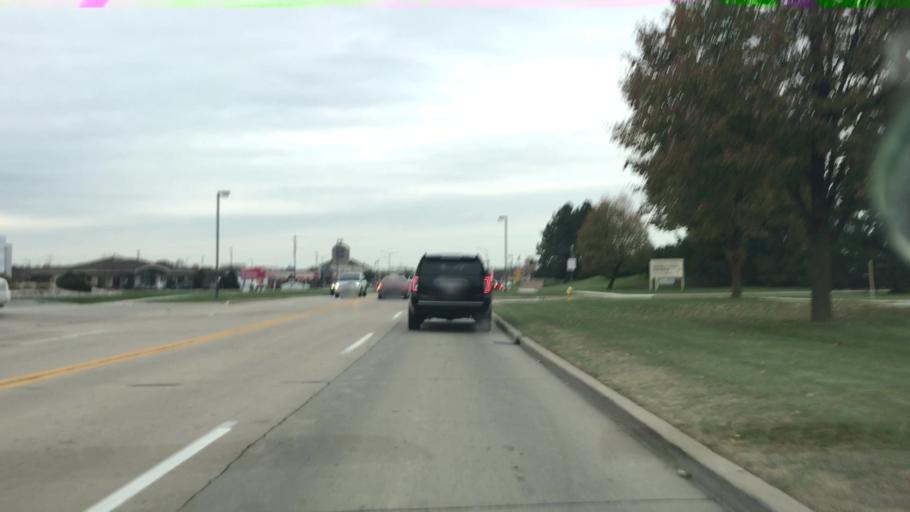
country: US
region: Wisconsin
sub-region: Brown County
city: De Pere
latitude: 44.4284
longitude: -88.1067
